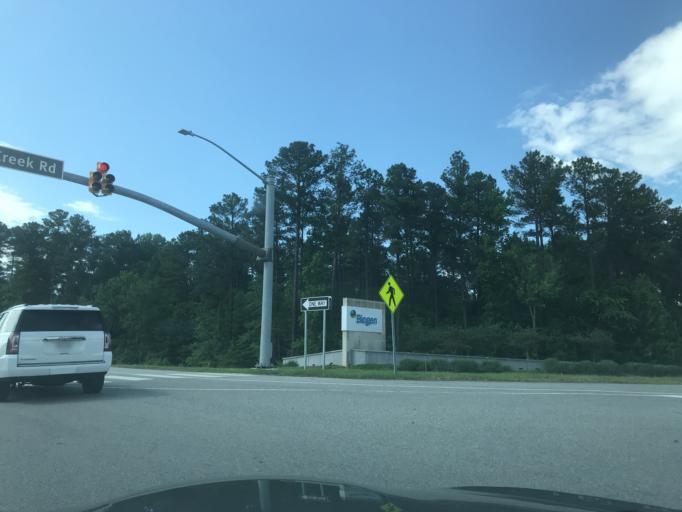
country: US
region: North Carolina
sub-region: Wake County
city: Morrisville
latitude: 35.8569
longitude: -78.8680
